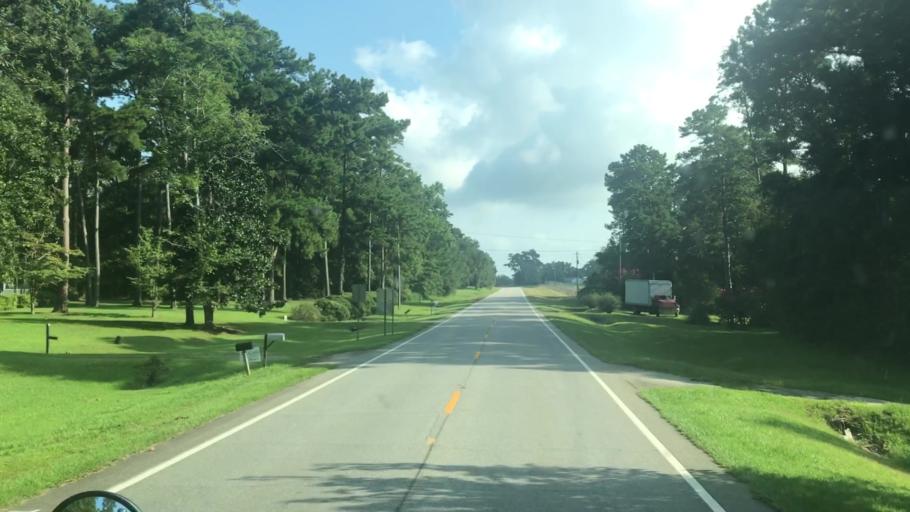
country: US
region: Florida
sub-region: Gadsden County
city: Havana
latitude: 30.7553
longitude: -84.4880
